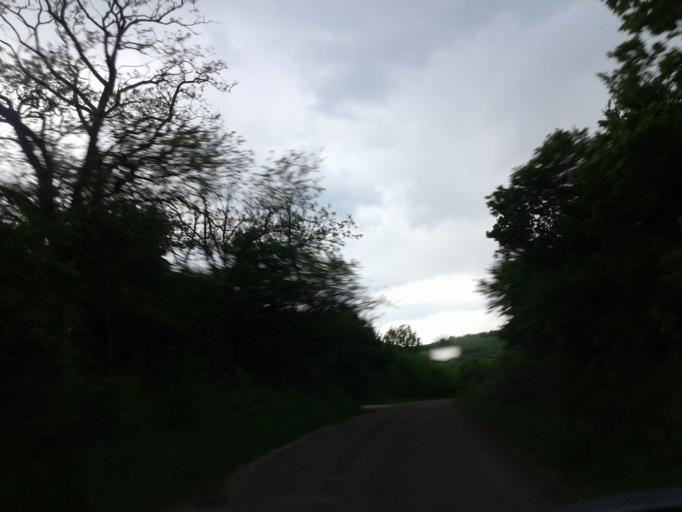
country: HU
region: Komarom-Esztergom
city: Kesztolc
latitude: 47.7103
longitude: 18.8194
